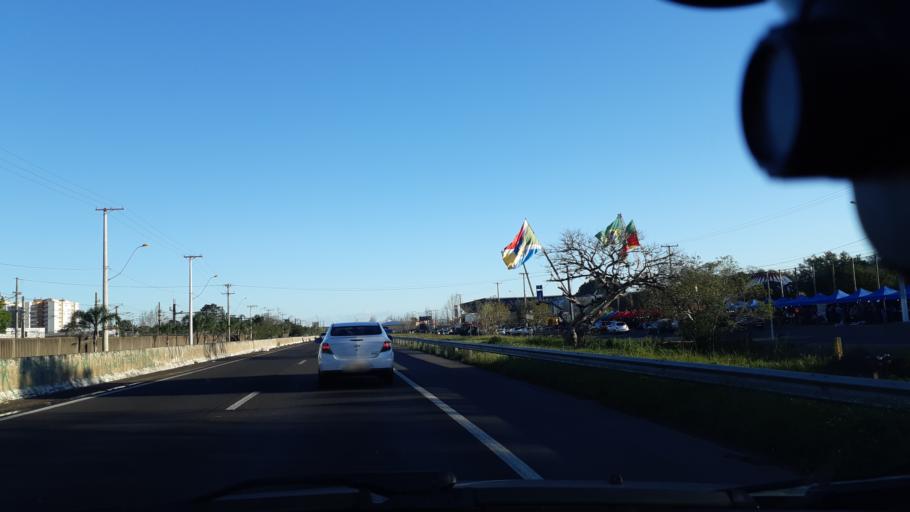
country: BR
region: Rio Grande do Sul
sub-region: Esteio
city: Esteio
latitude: -29.8524
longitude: -51.1798
